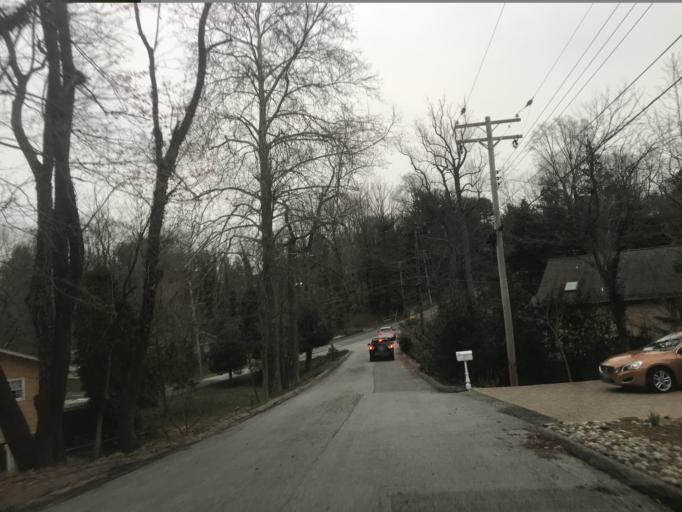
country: US
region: Maryland
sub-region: Anne Arundel County
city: Arnold
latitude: 39.0162
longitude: -76.5086
